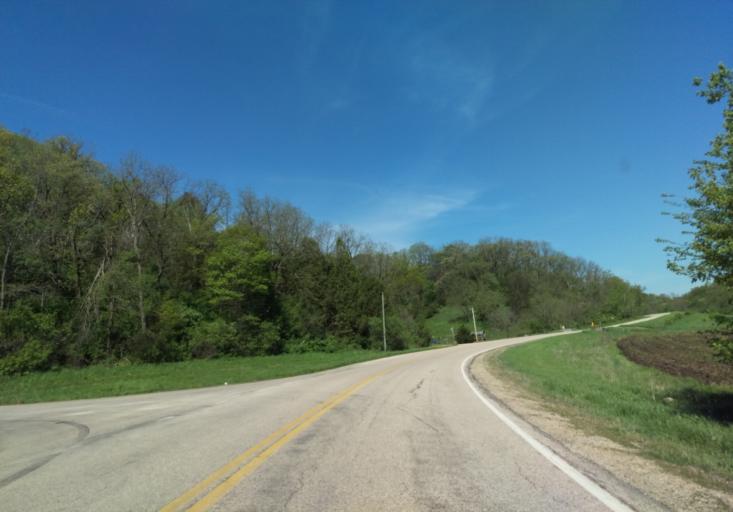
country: US
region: Wisconsin
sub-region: Dane County
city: Mount Horeb
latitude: 43.0594
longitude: -89.7845
